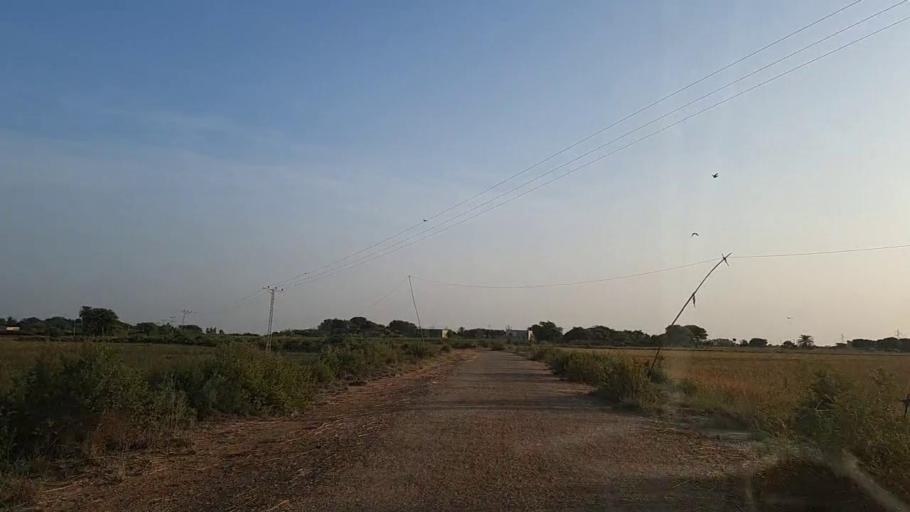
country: PK
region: Sindh
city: Daro Mehar
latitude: 24.6157
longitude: 68.0930
